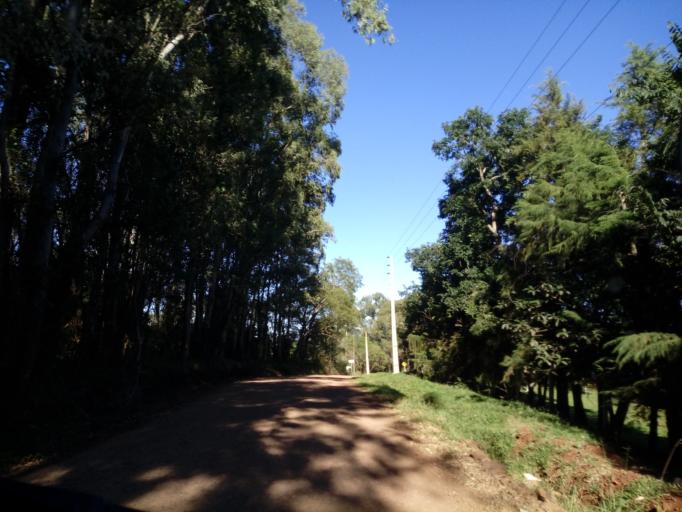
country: BR
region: Santa Catarina
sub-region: Chapeco
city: Chapeco
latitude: -27.2045
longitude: -52.6934
